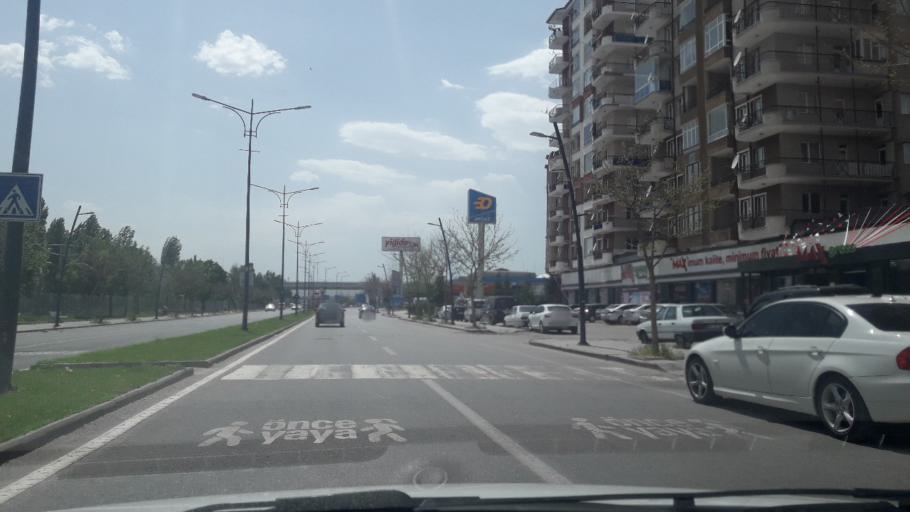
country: TR
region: Sivas
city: Sivas
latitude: 39.7264
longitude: 36.9717
